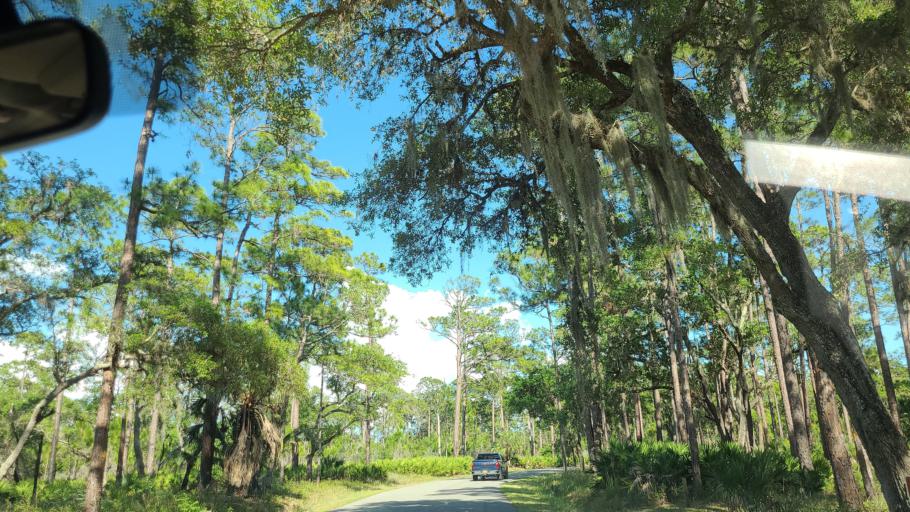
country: US
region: Florida
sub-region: Polk County
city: Babson Park
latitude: 27.9495
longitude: -81.3587
